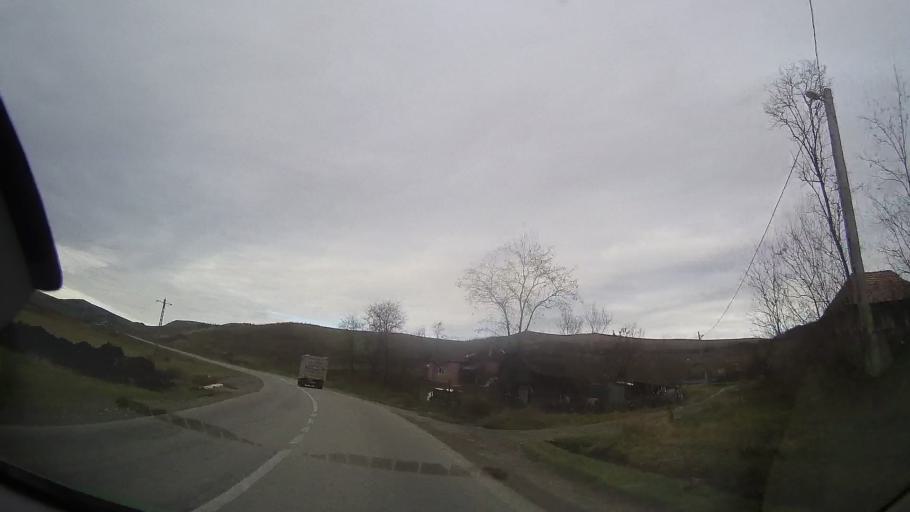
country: RO
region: Cluj
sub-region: Comuna Camarasu
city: Camarasu
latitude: 46.8007
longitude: 24.1636
